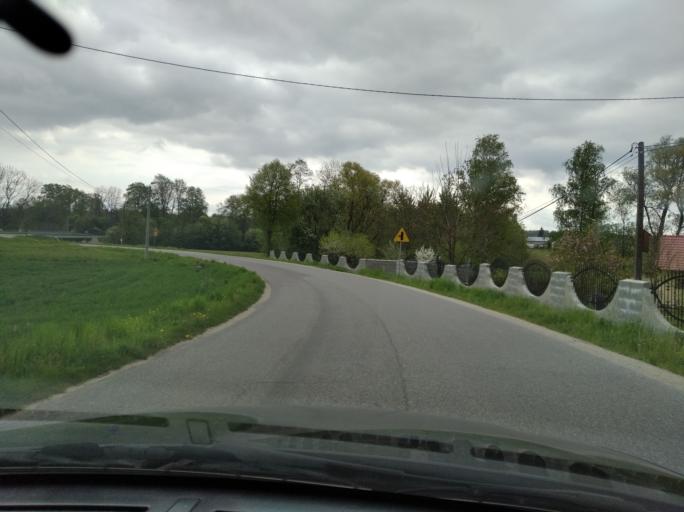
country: PL
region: Subcarpathian Voivodeship
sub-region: Powiat debicki
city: Leki Dolne
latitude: 49.9775
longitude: 21.2425
